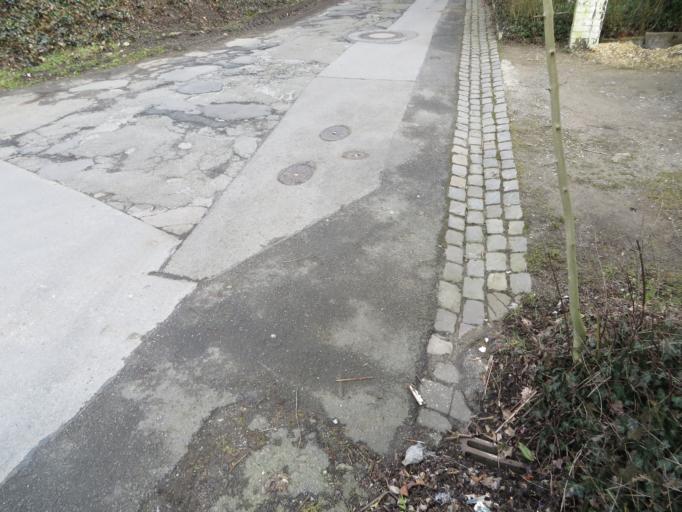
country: DE
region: North Rhine-Westphalia
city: Witten
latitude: 51.4219
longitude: 7.2857
